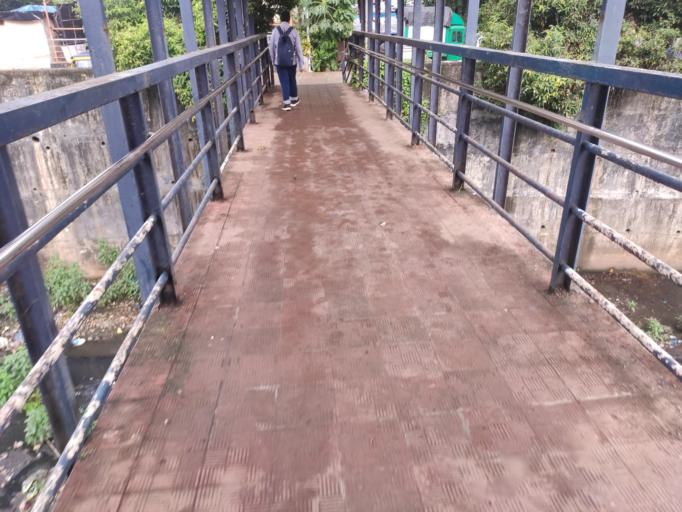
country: IN
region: Maharashtra
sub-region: Mumbai Suburban
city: Borivli
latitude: 19.2461
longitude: 72.8572
